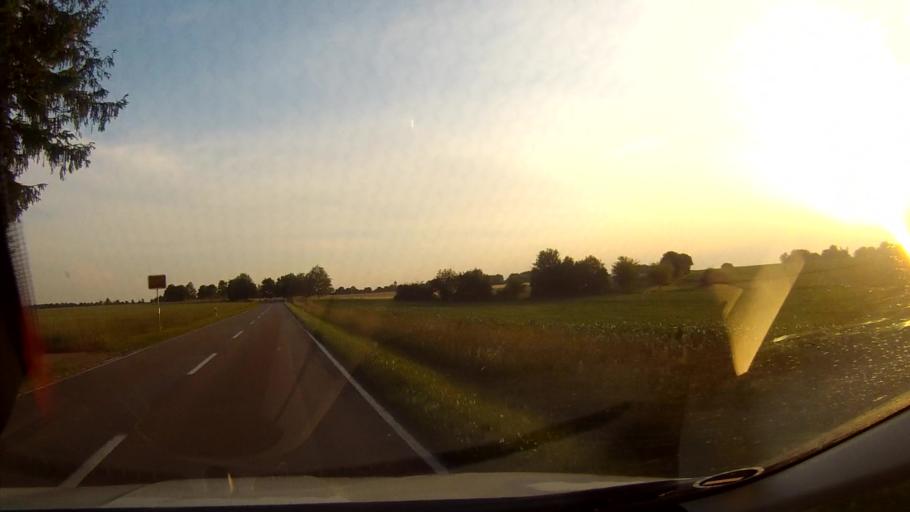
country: DE
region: Baden-Wuerttemberg
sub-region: Tuebingen Region
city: Staig
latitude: 48.2893
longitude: 9.9705
